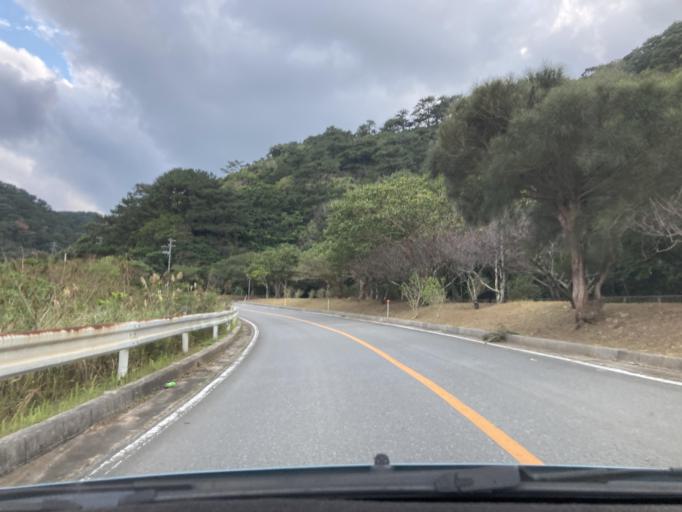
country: JP
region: Okinawa
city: Nago
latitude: 26.8360
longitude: 128.2866
